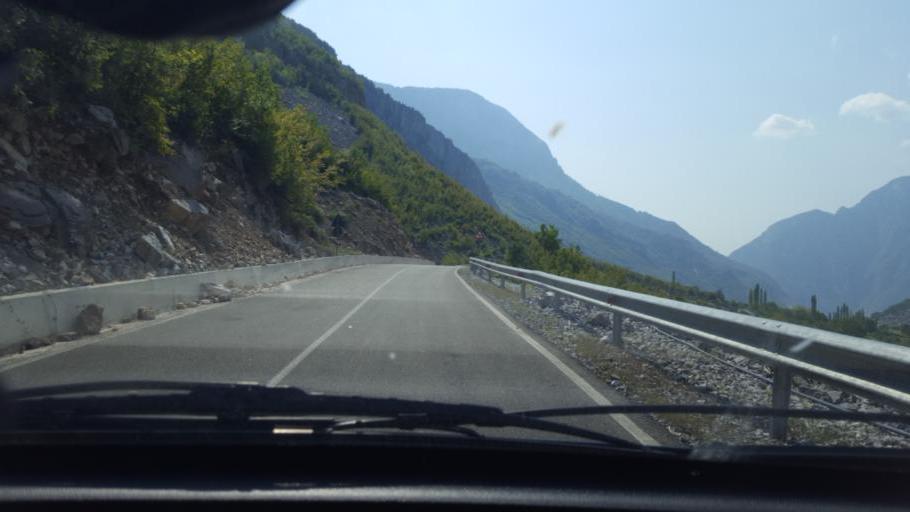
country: AL
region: Shkoder
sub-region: Rrethi i Malesia e Madhe
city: Kastrat
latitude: 42.5174
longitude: 19.6255
